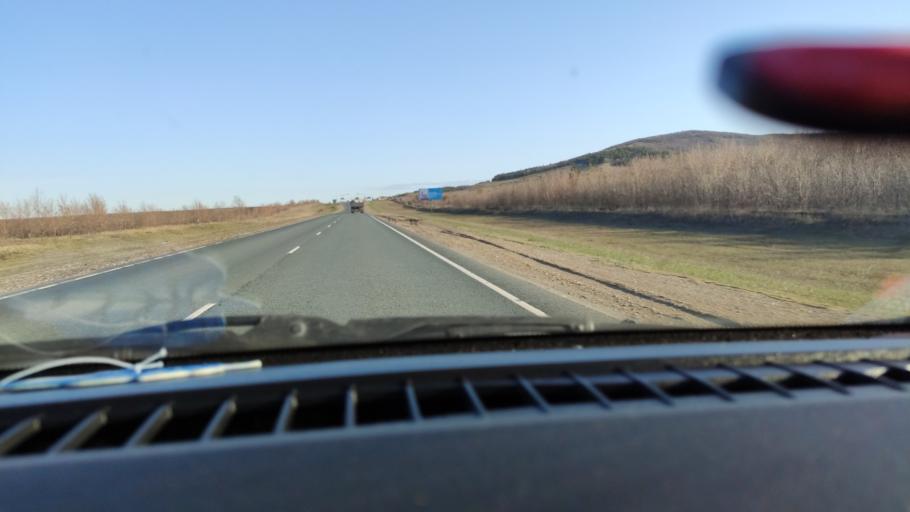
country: RU
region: Saratov
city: Alekseyevka
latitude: 52.2870
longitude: 47.9309
